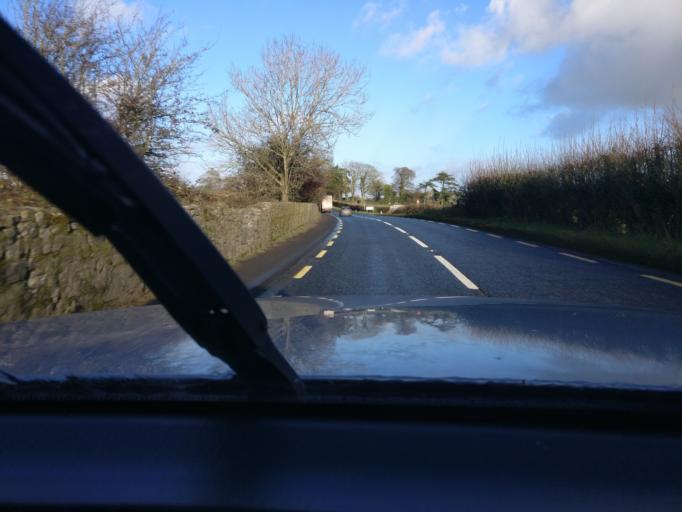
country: IE
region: Leinster
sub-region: An Iarmhi
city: Rathwire
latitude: 53.6052
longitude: -7.1010
